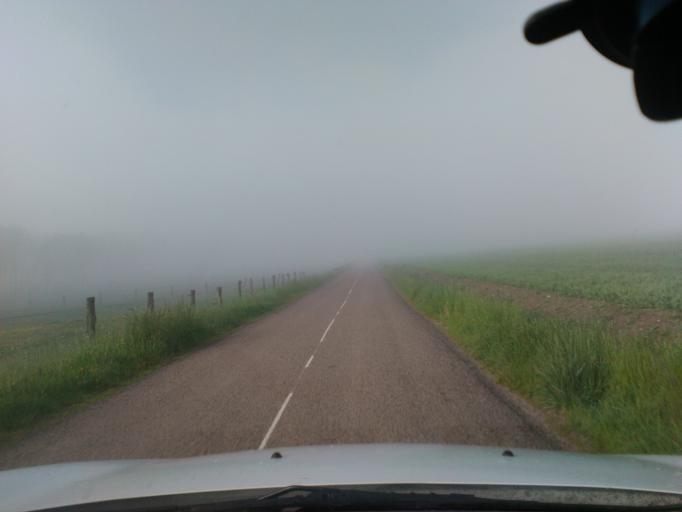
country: FR
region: Lorraine
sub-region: Departement des Vosges
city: Charmes
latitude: 48.3526
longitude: 6.2439
